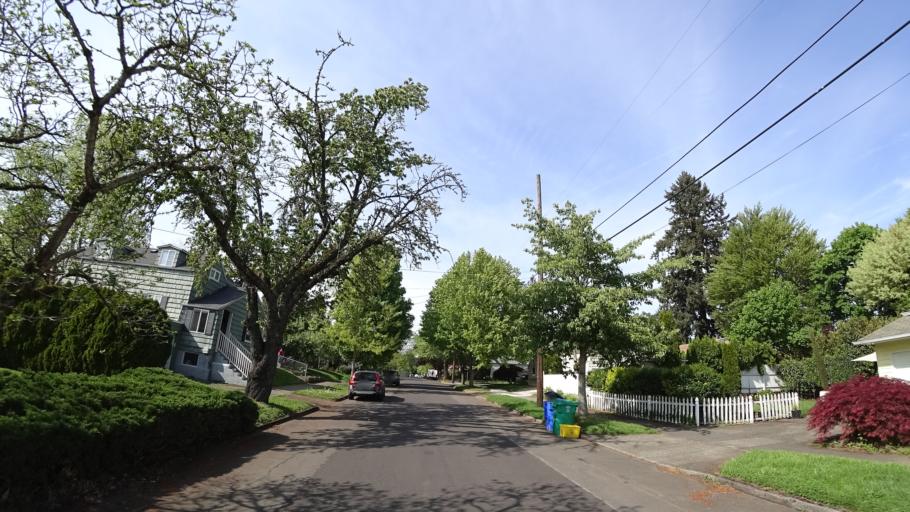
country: US
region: Oregon
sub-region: Clackamas County
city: Milwaukie
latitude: 45.4765
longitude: -122.6217
